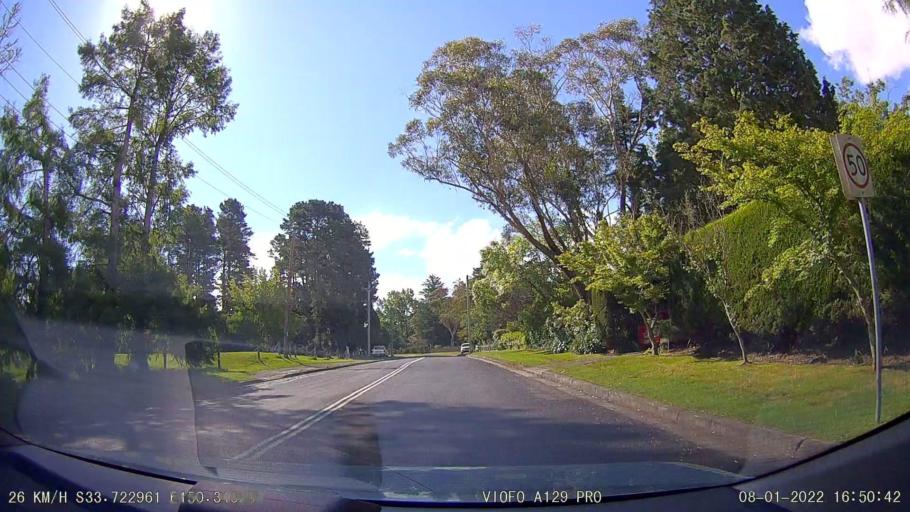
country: AU
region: New South Wales
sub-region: Blue Mountains Municipality
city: Leura
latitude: -33.7229
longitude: 150.3461
